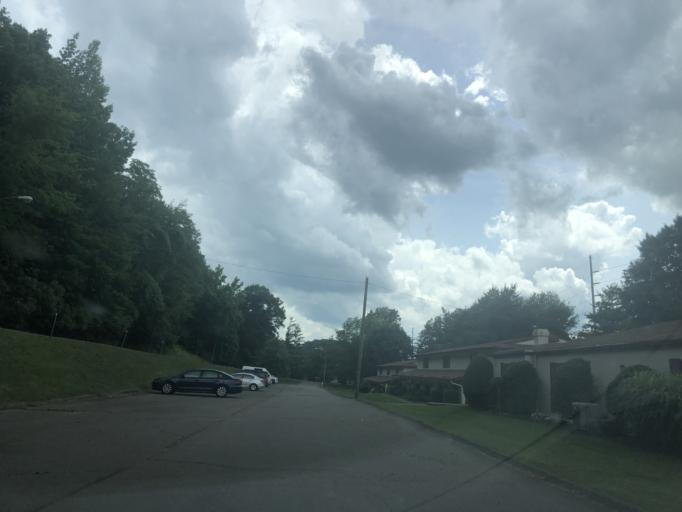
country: US
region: Tennessee
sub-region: Davidson County
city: Belle Meade
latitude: 36.0788
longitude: -86.9185
